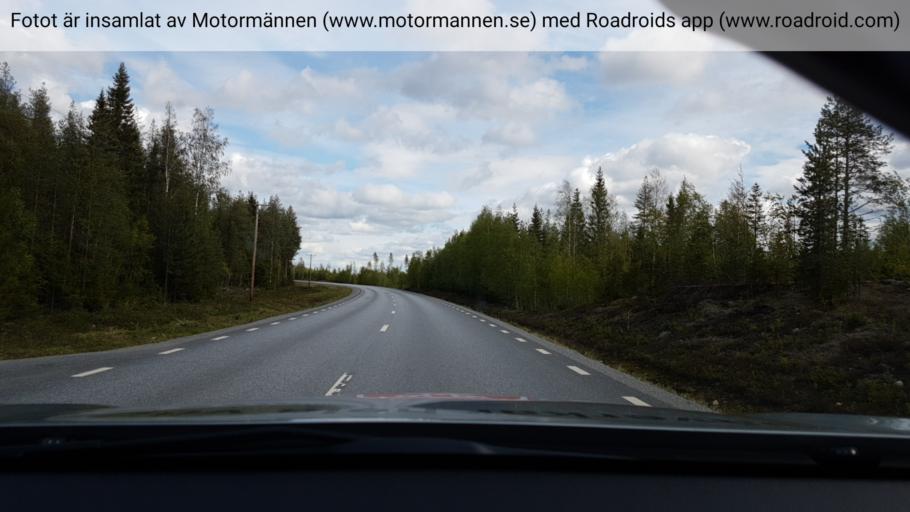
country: SE
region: Vaesternorrland
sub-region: OErnskoeldsviks Kommun
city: Bredbyn
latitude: 64.0843
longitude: 18.2195
